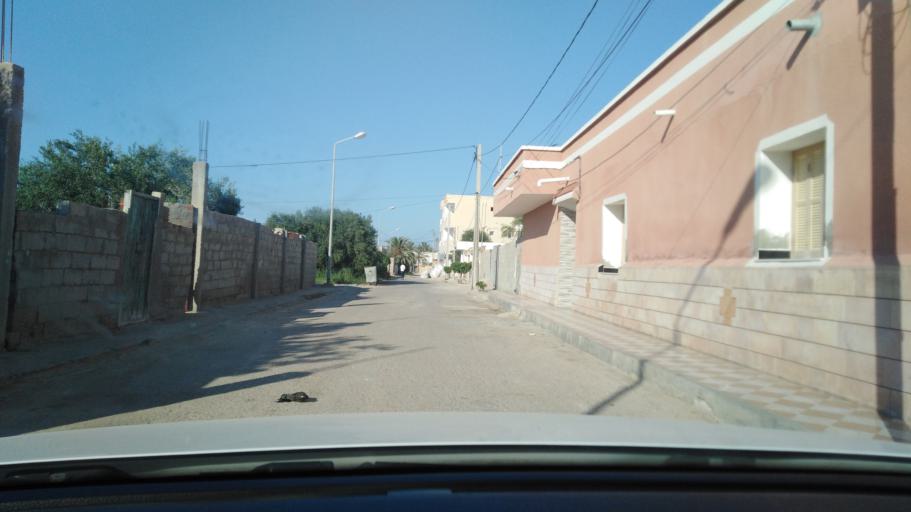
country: TN
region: Qabis
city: Gabes
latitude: 33.9370
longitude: 10.0724
